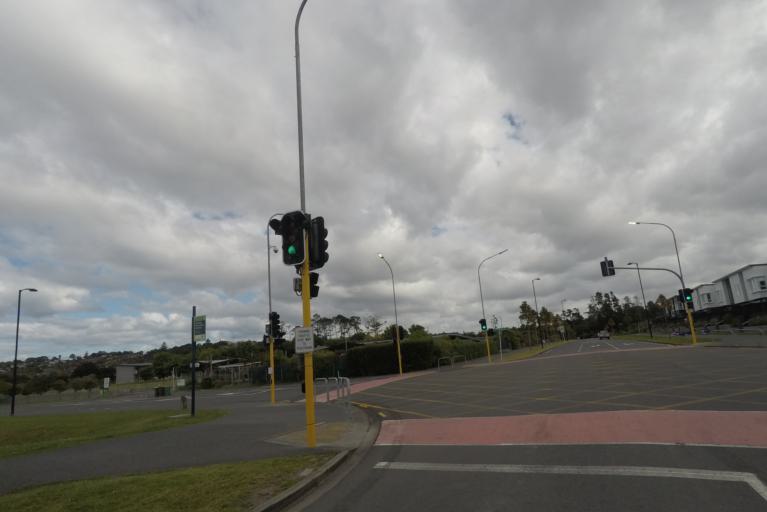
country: NZ
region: Auckland
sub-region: Auckland
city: Rothesay Bay
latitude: -36.6050
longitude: 174.6787
